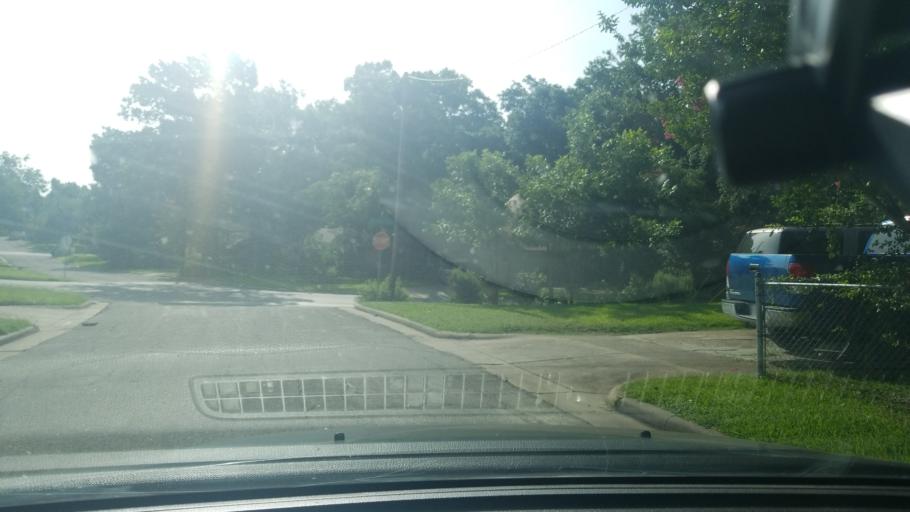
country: US
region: Texas
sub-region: Dallas County
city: Highland Park
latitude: 32.8020
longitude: -96.7102
